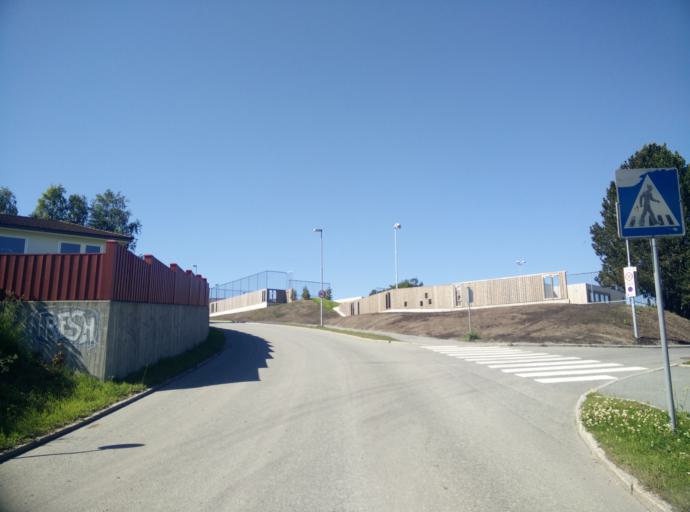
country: NO
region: Sor-Trondelag
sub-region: Trondheim
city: Trondheim
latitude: 63.4136
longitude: 10.3715
